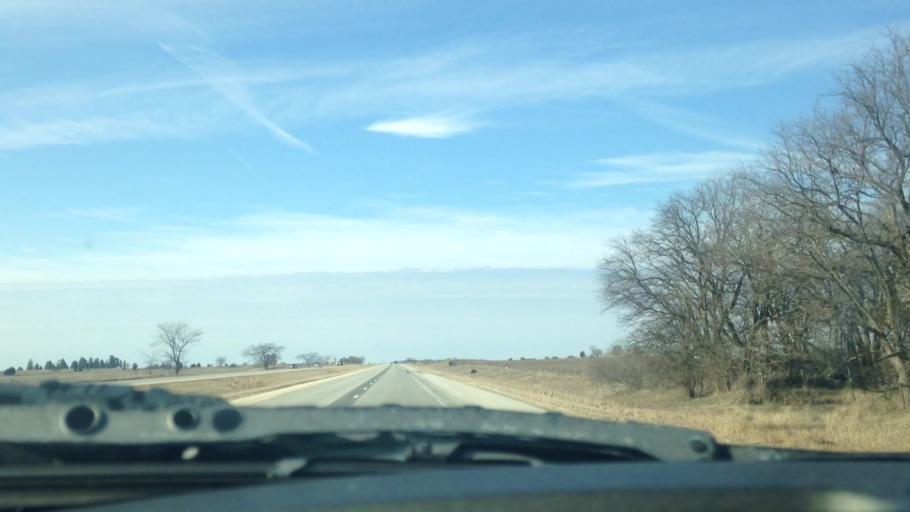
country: US
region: Illinois
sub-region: Ford County
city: Paxton
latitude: 40.5394
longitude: -88.0695
